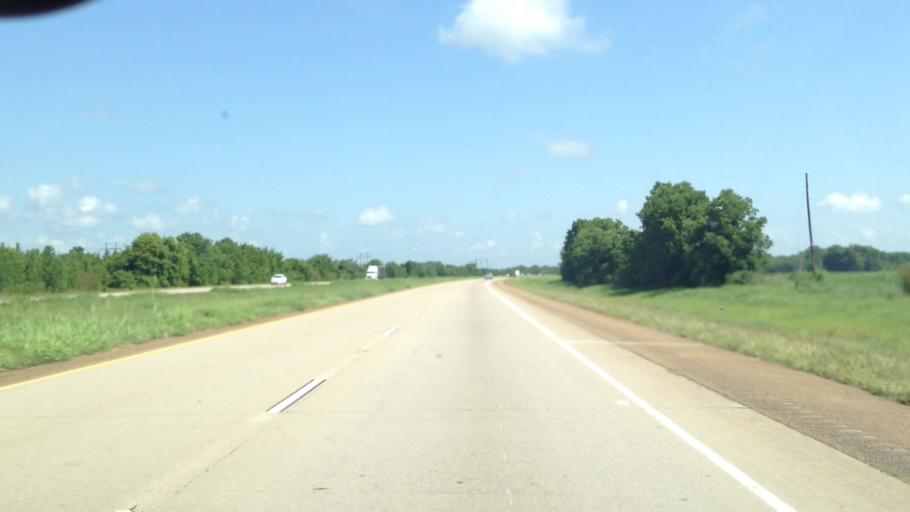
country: US
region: Louisiana
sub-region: Rapides Parish
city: Woodworth
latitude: 31.1834
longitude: -92.4701
